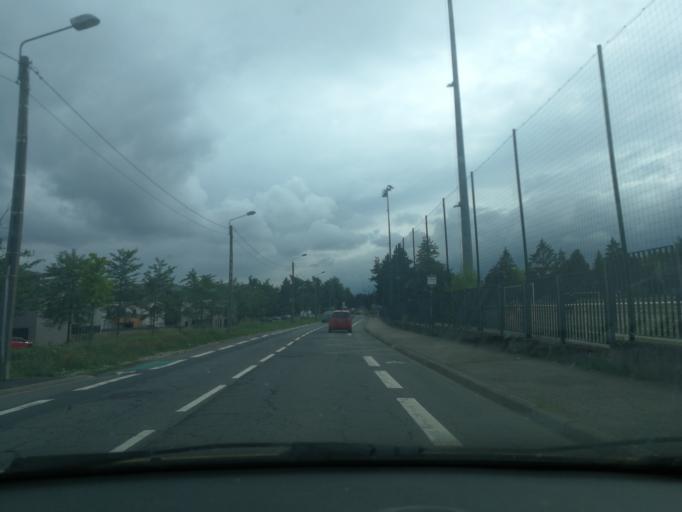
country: FR
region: Lorraine
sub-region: Departement de la Moselle
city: Terville
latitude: 49.3661
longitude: 6.1424
